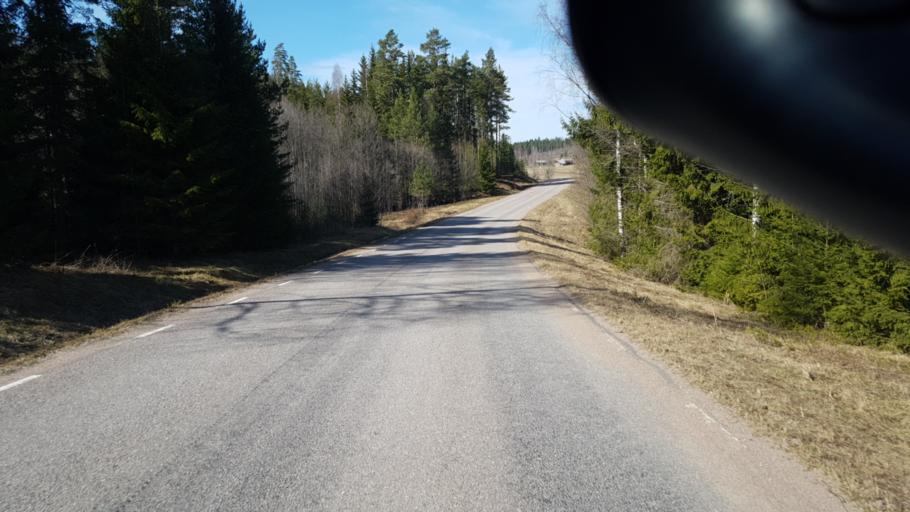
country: SE
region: Vaermland
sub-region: Arvika Kommun
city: Arvika
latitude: 59.6296
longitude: 12.7997
